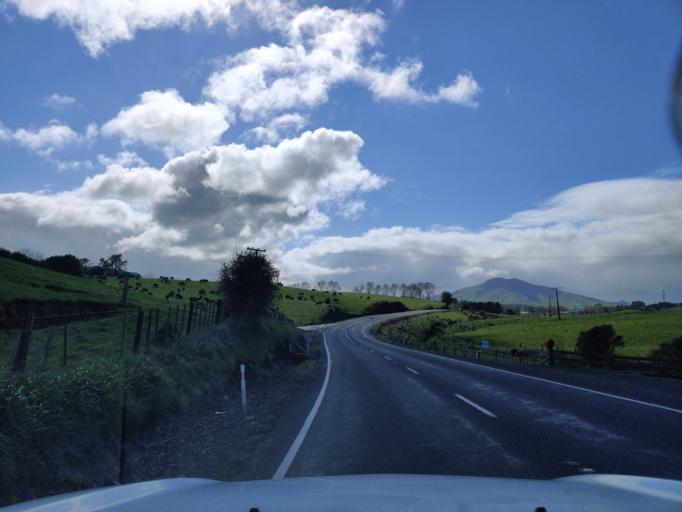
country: NZ
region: Waikato
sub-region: Otorohanga District
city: Otorohanga
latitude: -38.0682
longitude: 175.1631
